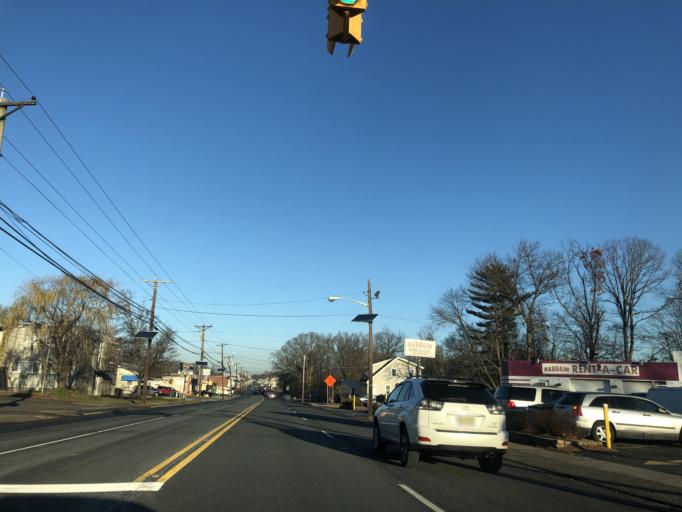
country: US
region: New Jersey
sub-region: Camden County
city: Somerdale
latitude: 39.8475
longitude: -75.0212
